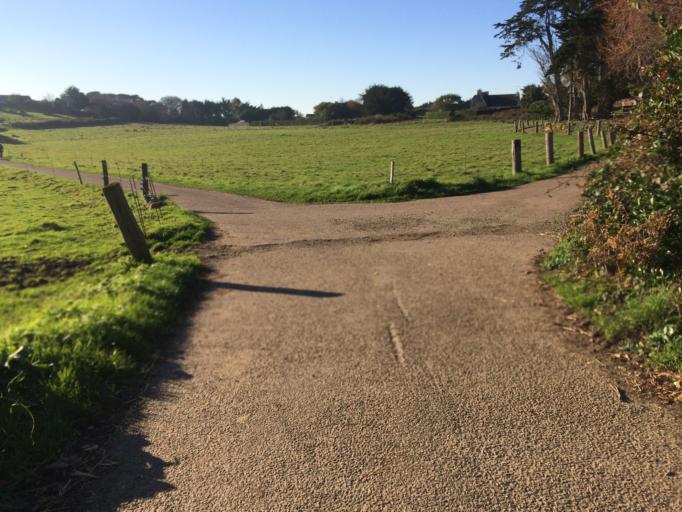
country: FR
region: Brittany
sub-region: Departement des Cotes-d'Armor
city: Ploubazlanec
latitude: 48.8576
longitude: -2.9970
